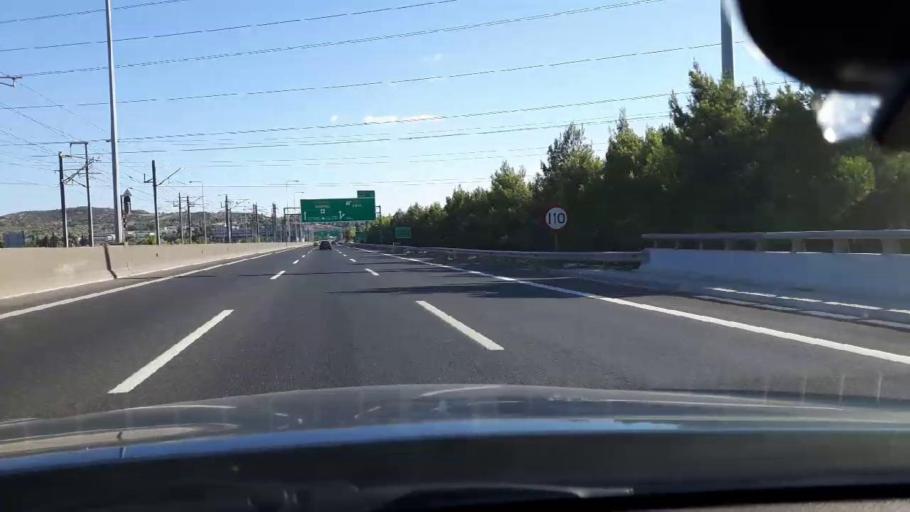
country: GR
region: Attica
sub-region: Nomarchia Anatolikis Attikis
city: Argithea
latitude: 37.9787
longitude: 23.8710
